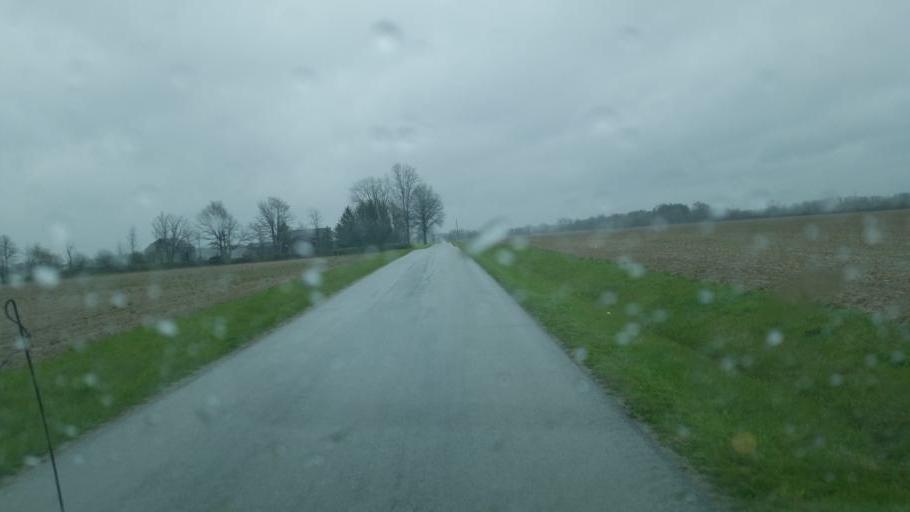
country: US
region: Ohio
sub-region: Wyandot County
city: Upper Sandusky
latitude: 40.8177
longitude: -83.3955
